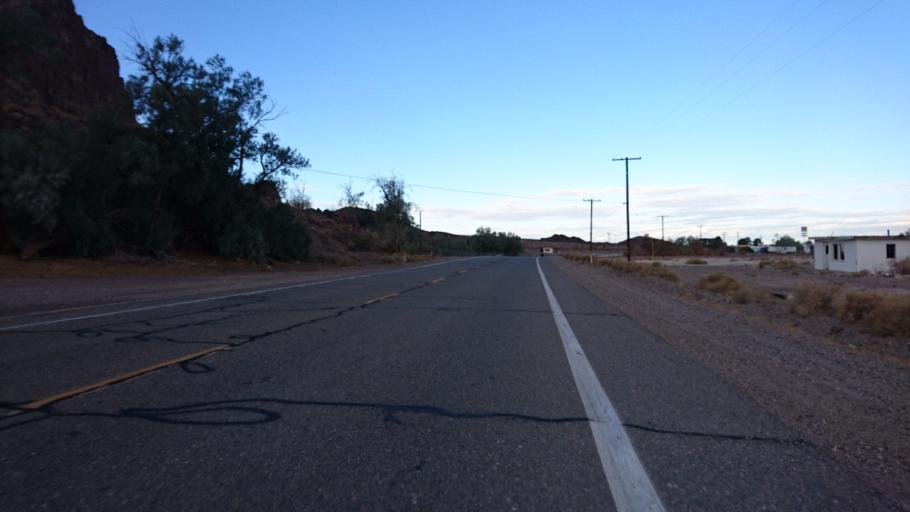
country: US
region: California
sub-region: San Bernardino County
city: Barstow
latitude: 34.8270
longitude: -116.6879
